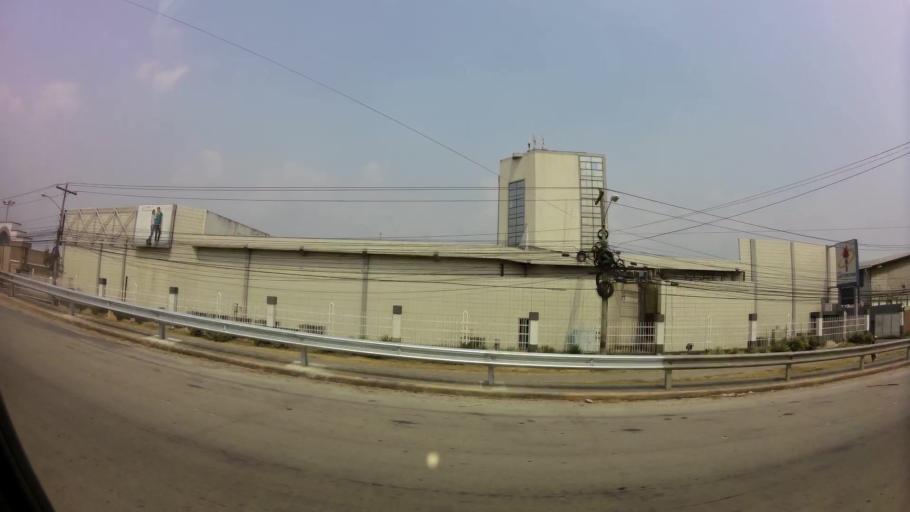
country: HN
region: Cortes
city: San Pedro Sula
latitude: 15.5031
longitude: -88.0042
